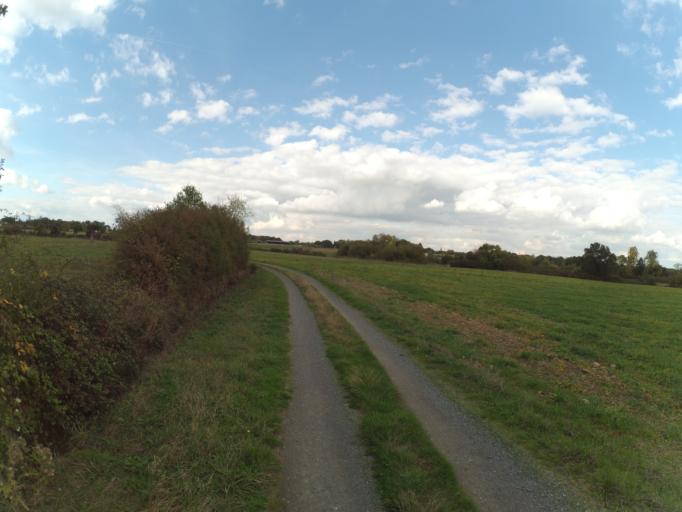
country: FR
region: Pays de la Loire
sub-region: Departement de la Loire-Atlantique
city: Saint-Lumine-de-Clisson
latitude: 47.0755
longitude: -1.3392
